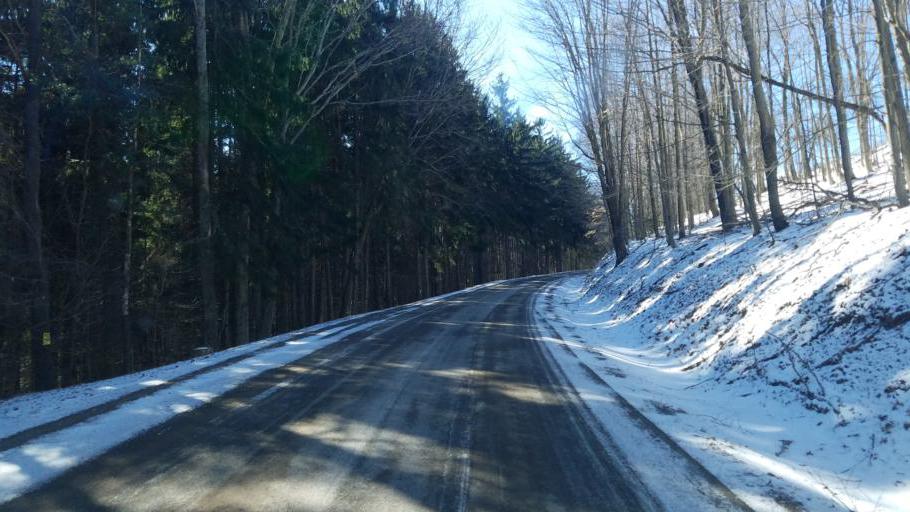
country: US
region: New York
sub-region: Allegany County
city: Wellsville
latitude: 42.0678
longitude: -78.0105
